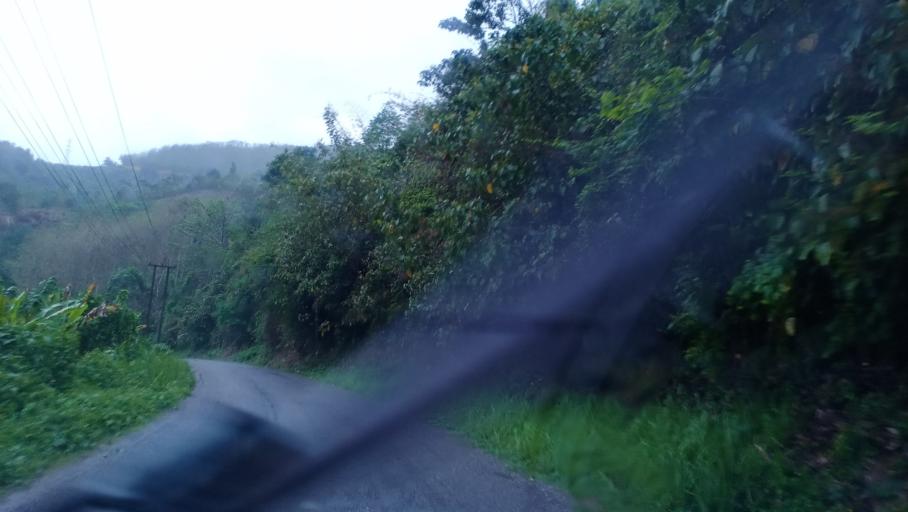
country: LA
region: Phongsali
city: Khoa
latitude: 21.0648
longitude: 102.4783
